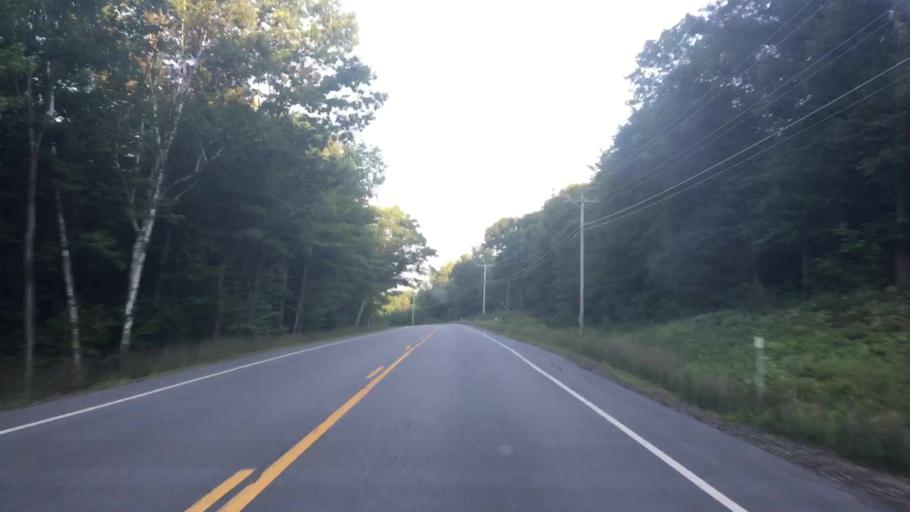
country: US
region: New Hampshire
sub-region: Belknap County
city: Gilmanton
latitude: 43.4305
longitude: -71.3907
